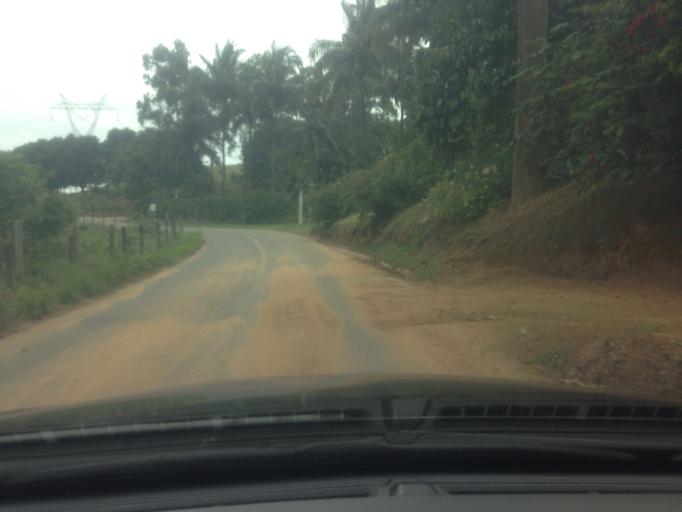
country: BR
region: Espirito Santo
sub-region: Guarapari
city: Guarapari
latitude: -20.6216
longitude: -40.5289
